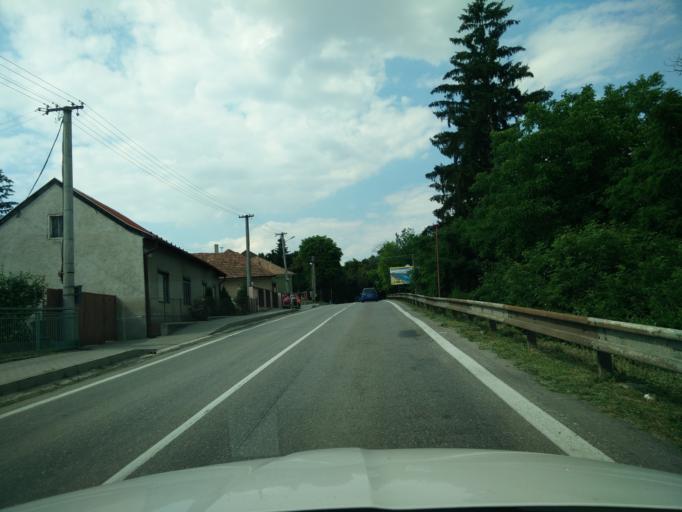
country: SK
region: Nitriansky
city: Partizanske
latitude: 48.6223
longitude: 18.3031
